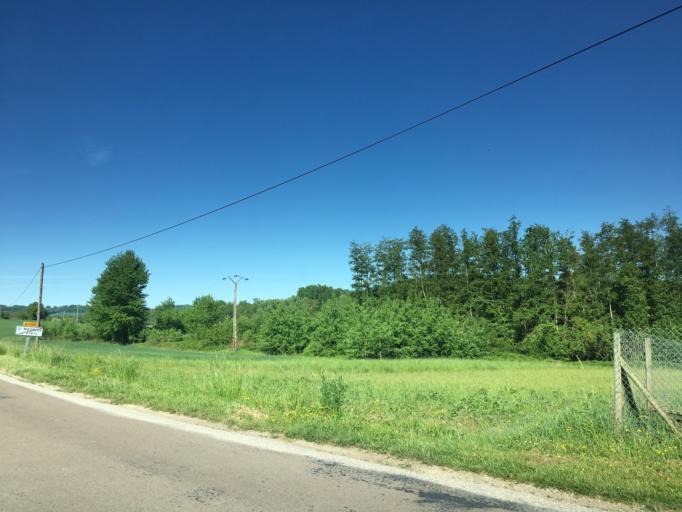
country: FR
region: Bourgogne
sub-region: Departement de l'Yonne
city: Aillant-sur-Tholon
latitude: 47.8210
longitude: 3.3471
